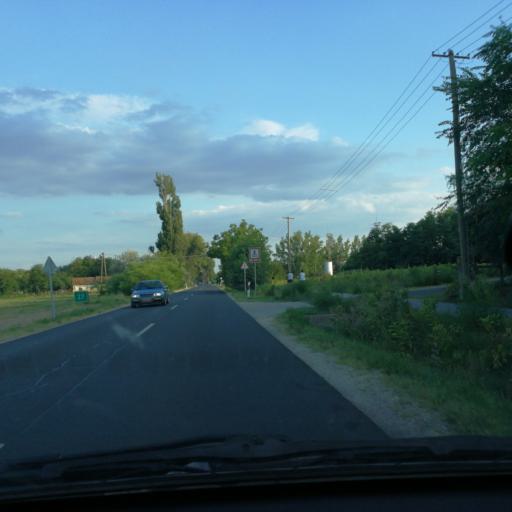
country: HU
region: Bacs-Kiskun
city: Kiskunmajsa
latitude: 46.5267
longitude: 19.7437
